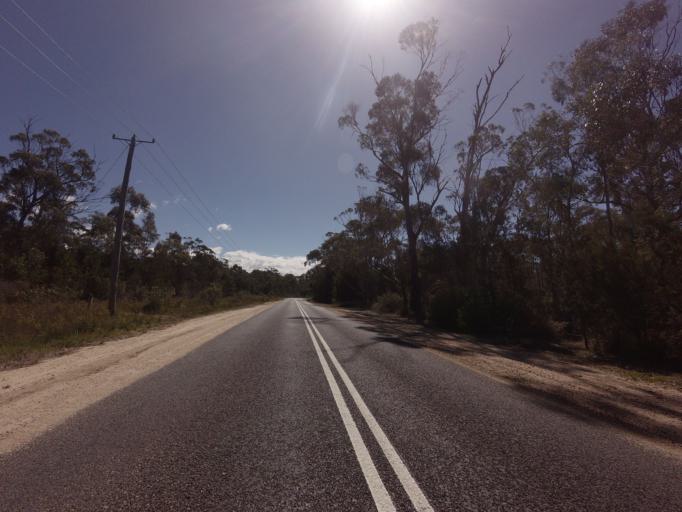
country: AU
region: Tasmania
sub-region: Break O'Day
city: St Helens
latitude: -41.8425
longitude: 148.2545
